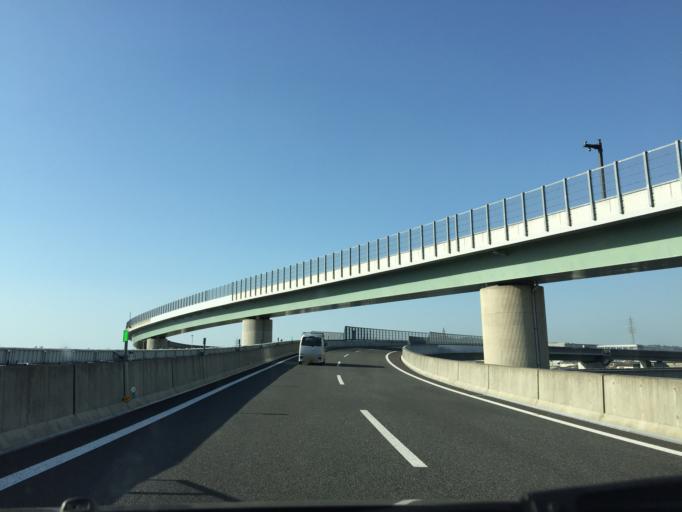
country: JP
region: Shizuoka
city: Shizuoka-shi
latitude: 35.0482
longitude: 138.4880
